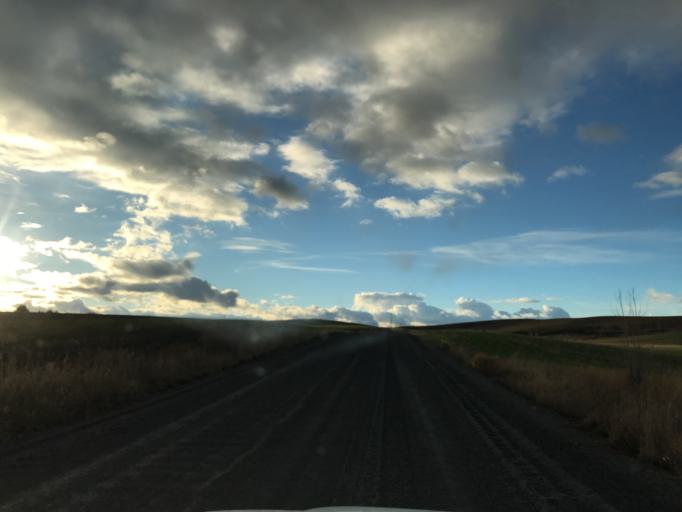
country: US
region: Idaho
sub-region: Latah County
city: Moscow
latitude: 46.7732
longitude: -116.9750
